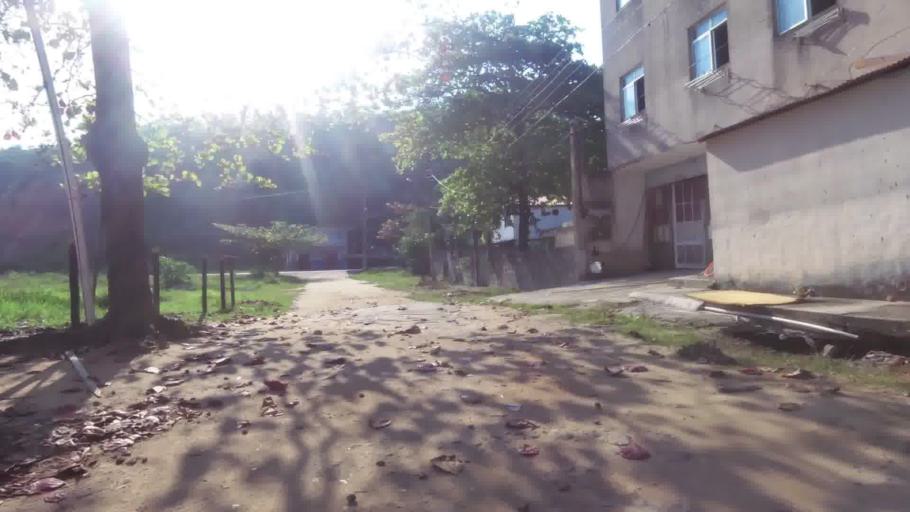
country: BR
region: Espirito Santo
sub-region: Piuma
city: Piuma
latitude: -20.8596
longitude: -40.7559
